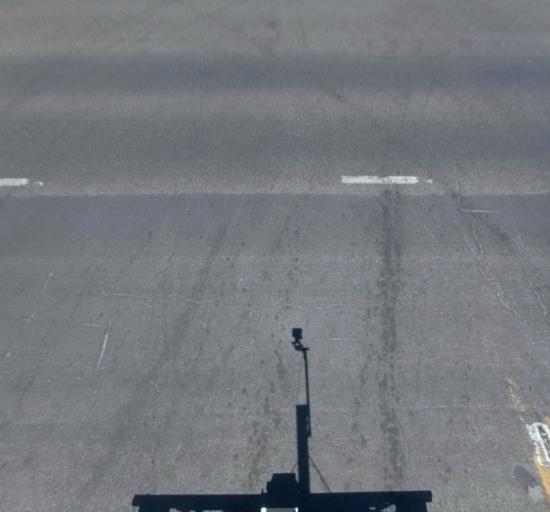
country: US
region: California
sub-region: Madera County
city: Chowchilla
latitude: 37.0838
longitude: -120.2568
